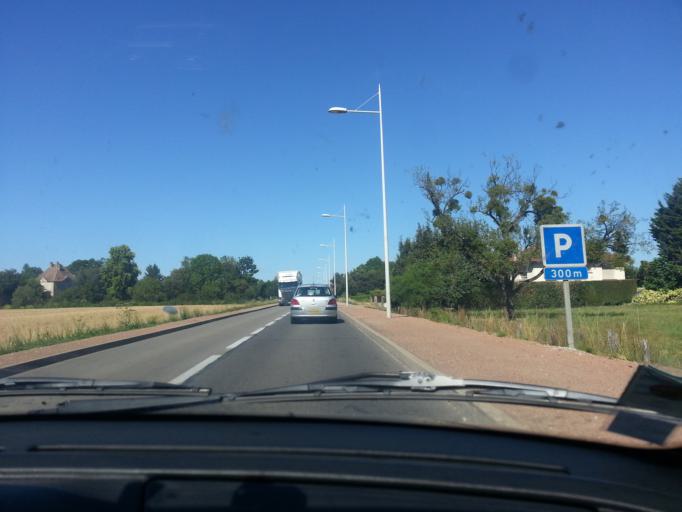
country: FR
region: Bourgogne
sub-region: Departement de Saone-et-Loire
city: Sassenay
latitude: 46.8173
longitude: 4.9636
